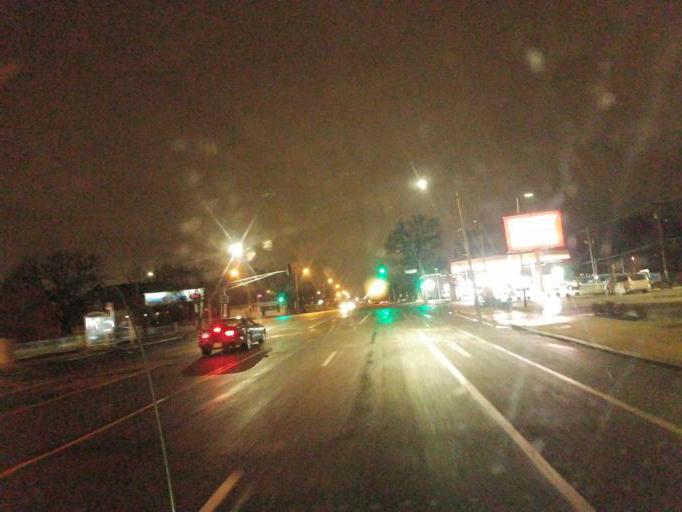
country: US
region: Missouri
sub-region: City of Saint Louis
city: St. Louis
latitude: 38.6500
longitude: -90.1996
